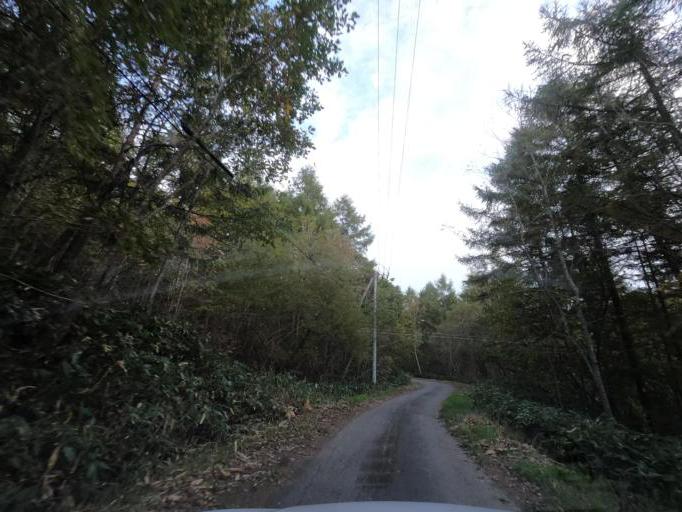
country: JP
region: Hokkaido
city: Obihiro
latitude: 42.5879
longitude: 143.3138
